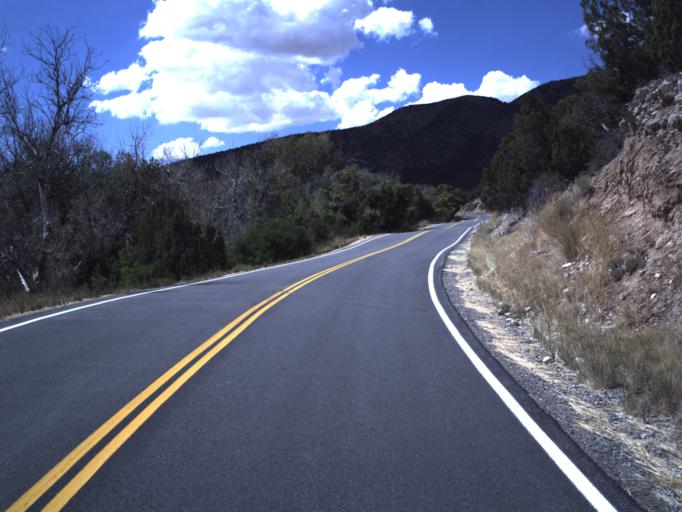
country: US
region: Utah
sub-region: Tooele County
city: Grantsville
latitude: 40.3430
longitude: -112.5432
